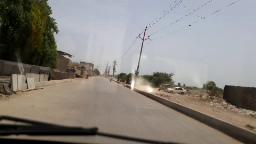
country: PK
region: Sindh
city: Malir Cantonment
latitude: 24.8362
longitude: 67.2052
